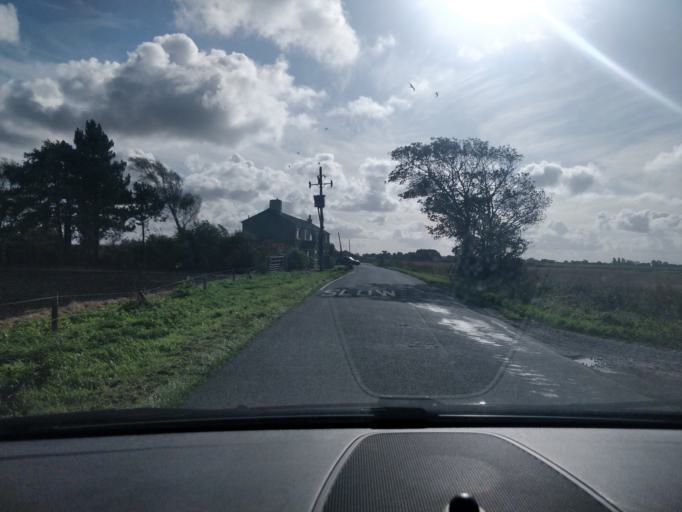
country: GB
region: England
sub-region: Lancashire
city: Banks
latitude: 53.6288
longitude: -2.9415
